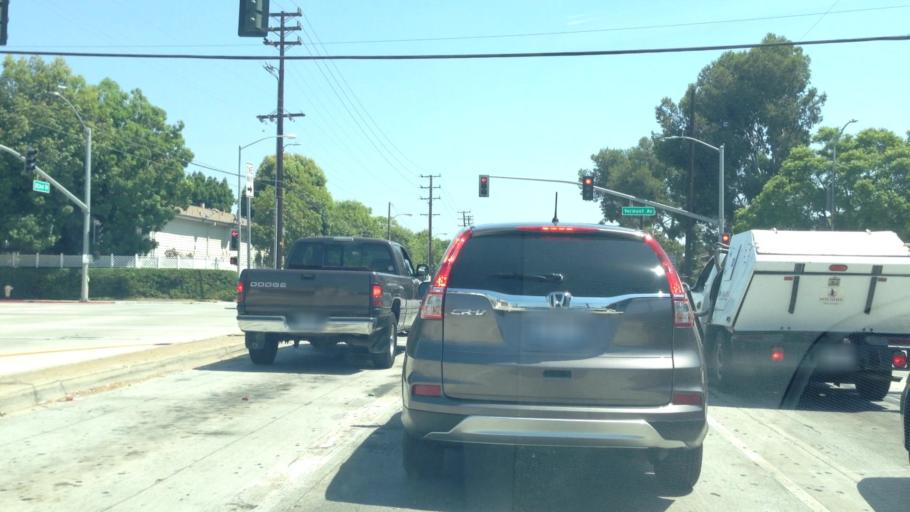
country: US
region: California
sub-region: Los Angeles County
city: West Carson
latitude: 33.8244
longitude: -118.2907
